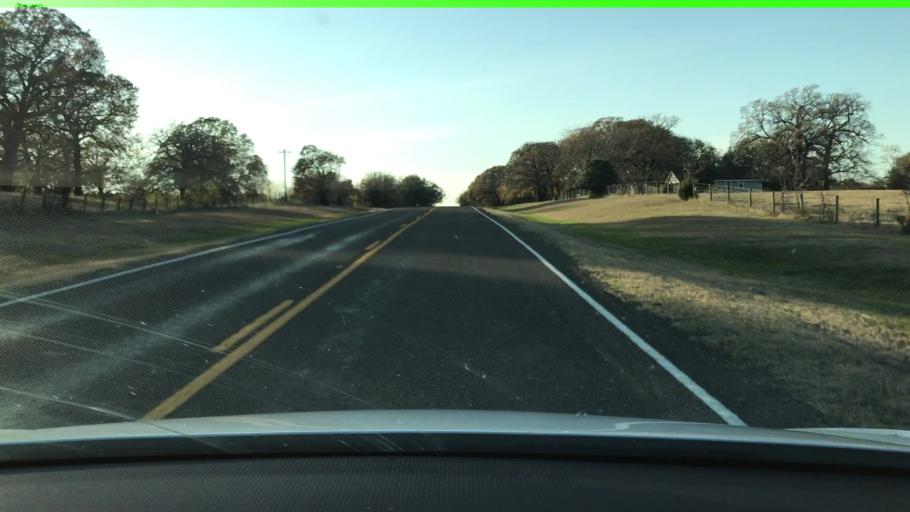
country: US
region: Texas
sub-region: Kaufman County
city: Kemp
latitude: 32.5711
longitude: -96.1483
